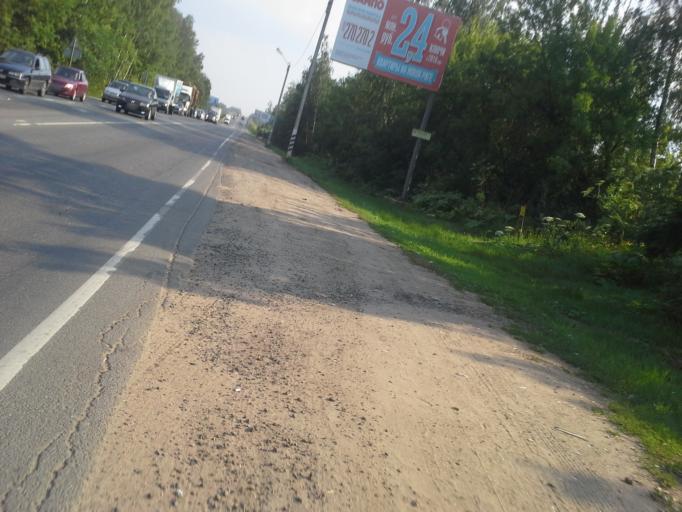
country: RU
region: Moskovskaya
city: Istra
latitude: 55.9035
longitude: 36.9449
